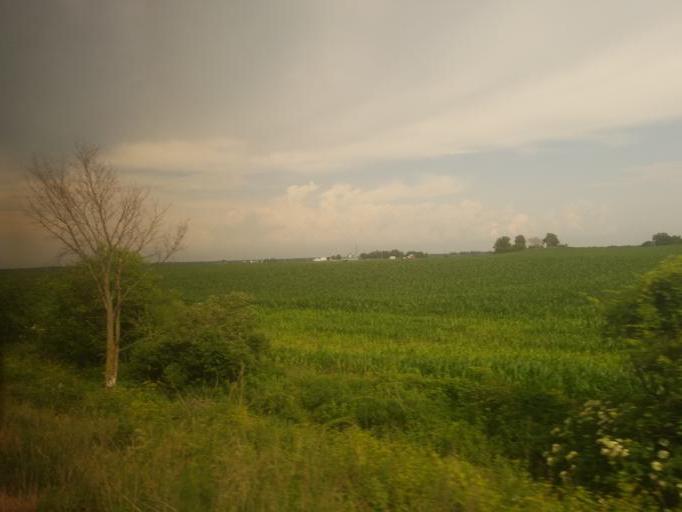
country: US
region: Illinois
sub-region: Bureau County
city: Princeton
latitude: 41.3717
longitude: -89.5628
